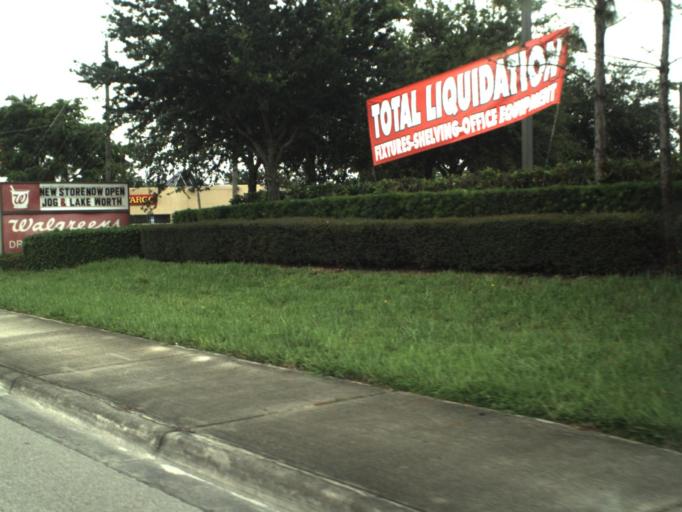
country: US
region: Florida
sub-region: Palm Beach County
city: Greenacres City
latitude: 26.6176
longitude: -80.1646
